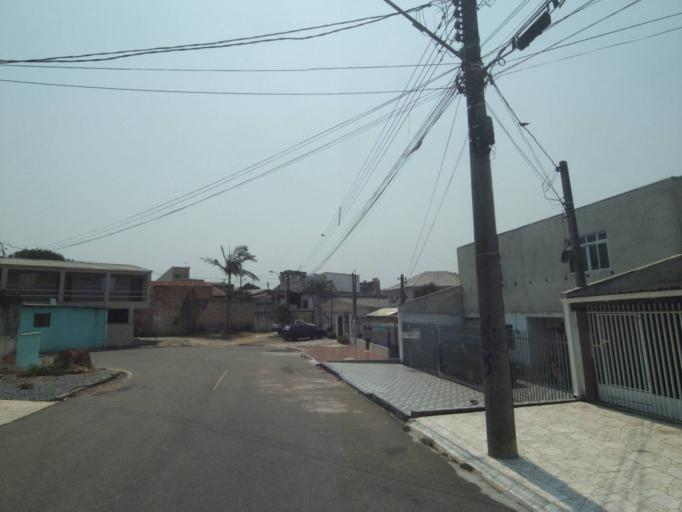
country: BR
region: Parana
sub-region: Sao Jose Dos Pinhais
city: Sao Jose dos Pinhais
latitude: -25.5281
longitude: -49.2454
